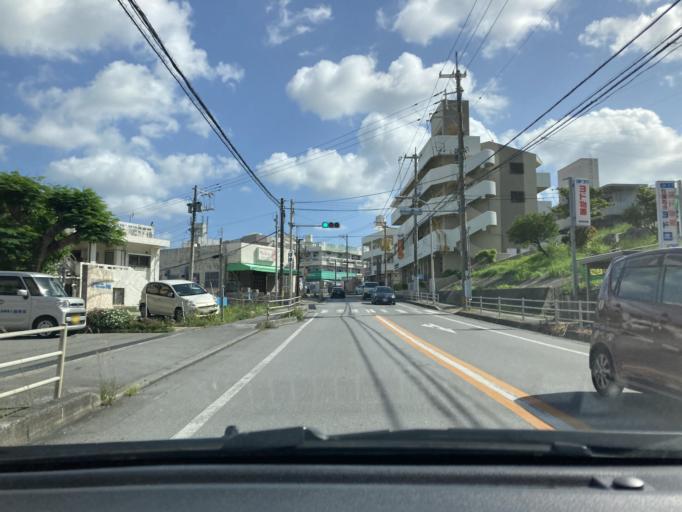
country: JP
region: Okinawa
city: Tomigusuku
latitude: 26.1916
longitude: 127.6785
